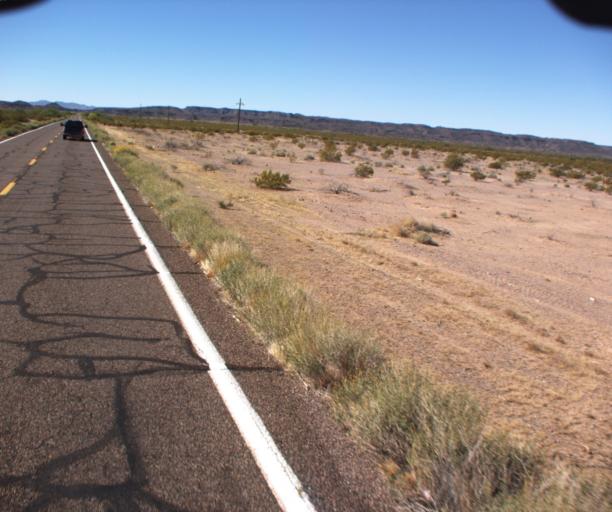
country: US
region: Arizona
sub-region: Pima County
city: Ajo
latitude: 32.6042
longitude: -112.8697
